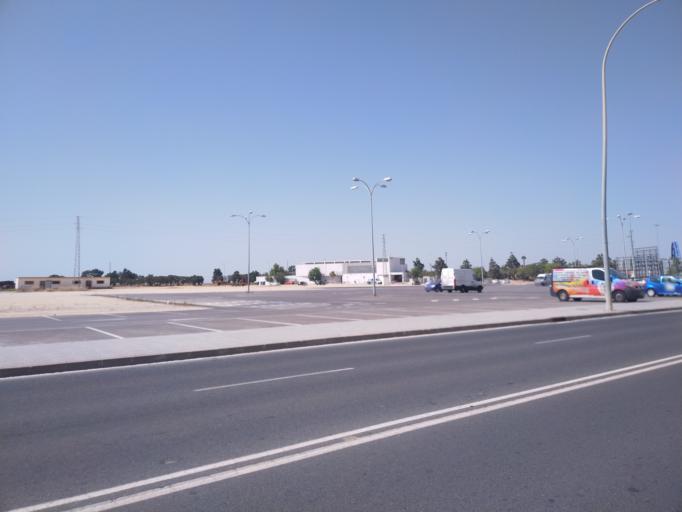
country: ES
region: Andalusia
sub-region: Provincia de Cadiz
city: Chiclana de la Frontera
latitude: 36.4220
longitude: -6.1551
